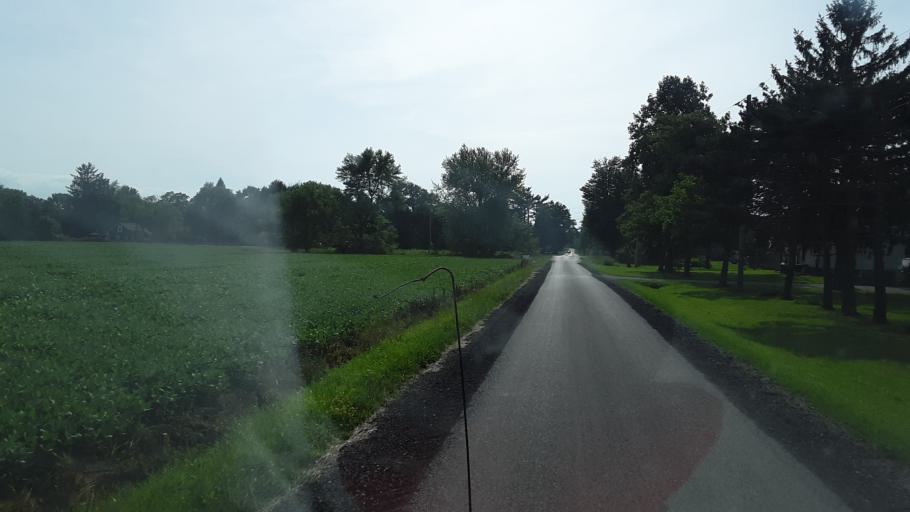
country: US
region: Ohio
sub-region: Ashtabula County
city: Jefferson
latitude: 41.6912
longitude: -80.6654
